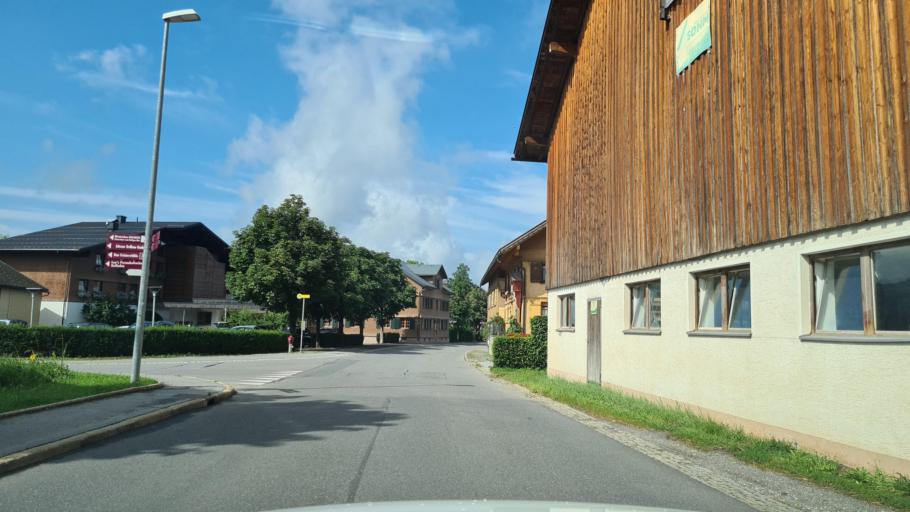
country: AT
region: Vorarlberg
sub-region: Politischer Bezirk Bregenz
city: Krumbach
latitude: 47.4567
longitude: 9.9652
